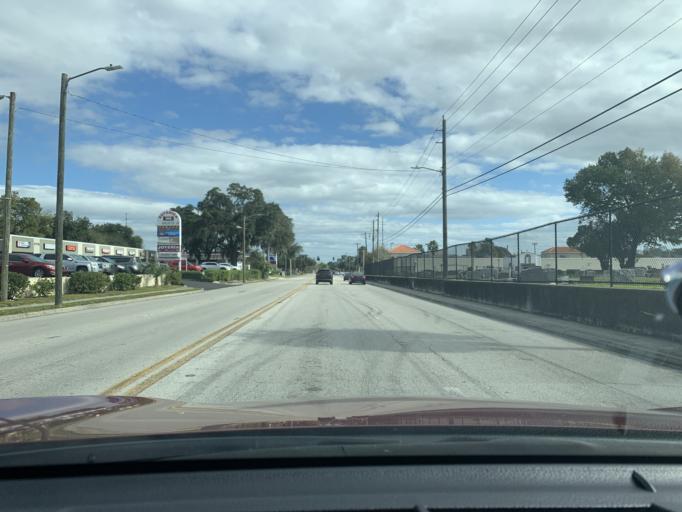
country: US
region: Florida
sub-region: Hillsborough County
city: Tampa
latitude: 27.9667
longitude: -82.4950
